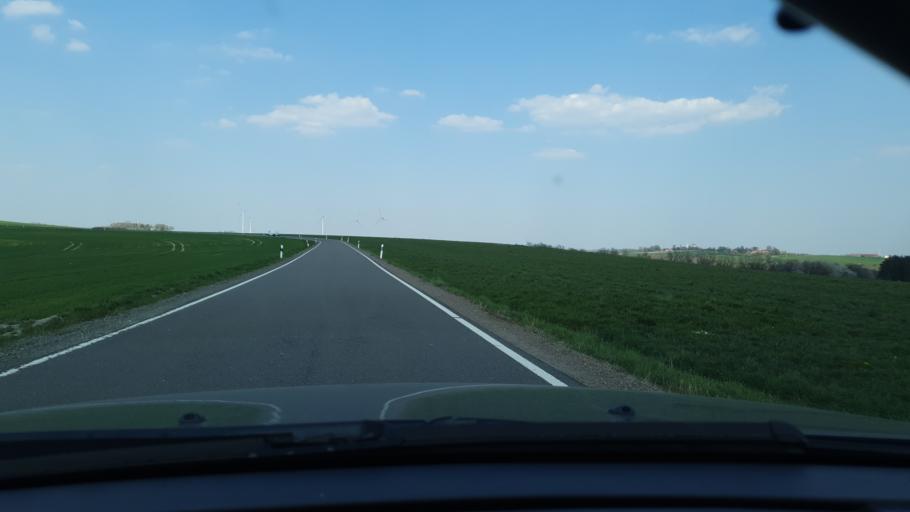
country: DE
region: Rheinland-Pfalz
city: Knopp-Labach
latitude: 49.3467
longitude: 7.4886
